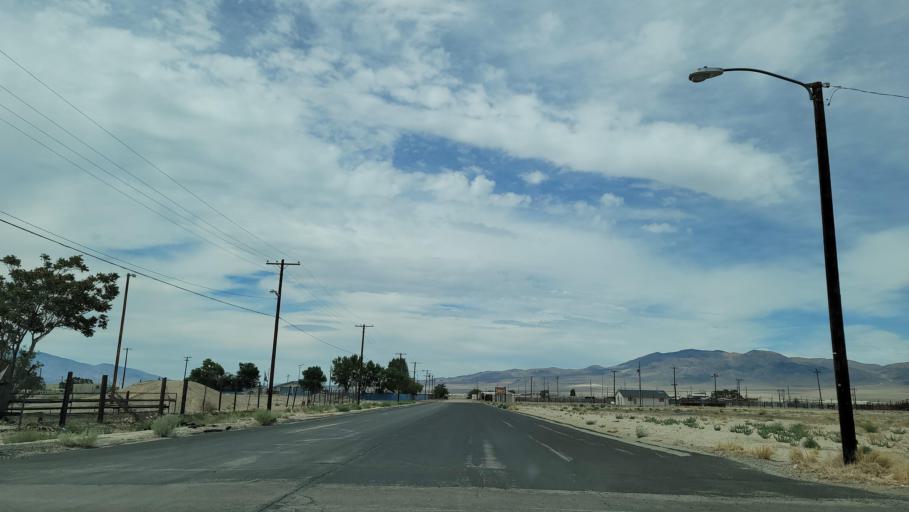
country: US
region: Nevada
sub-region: Mineral County
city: Hawthorne
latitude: 38.5276
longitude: -118.6161
